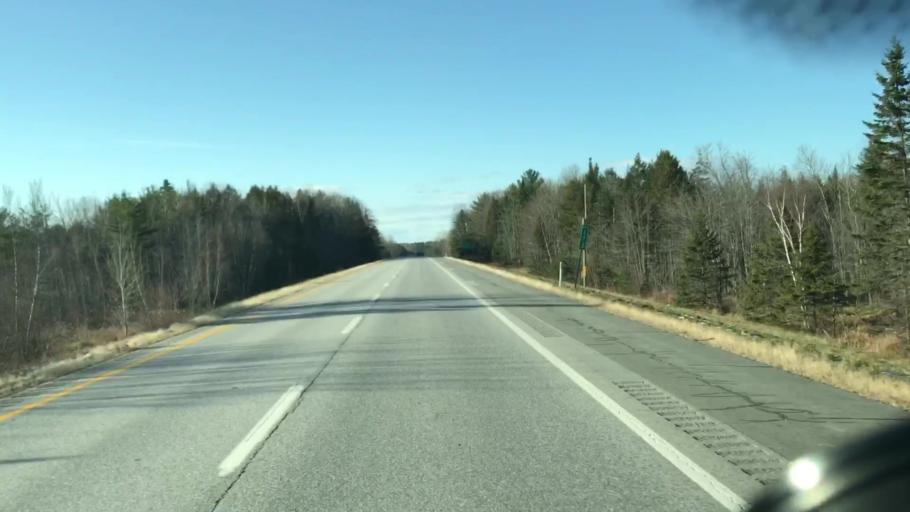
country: US
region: Maine
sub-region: Penobscot County
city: Carmel
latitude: 44.7642
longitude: -68.9885
